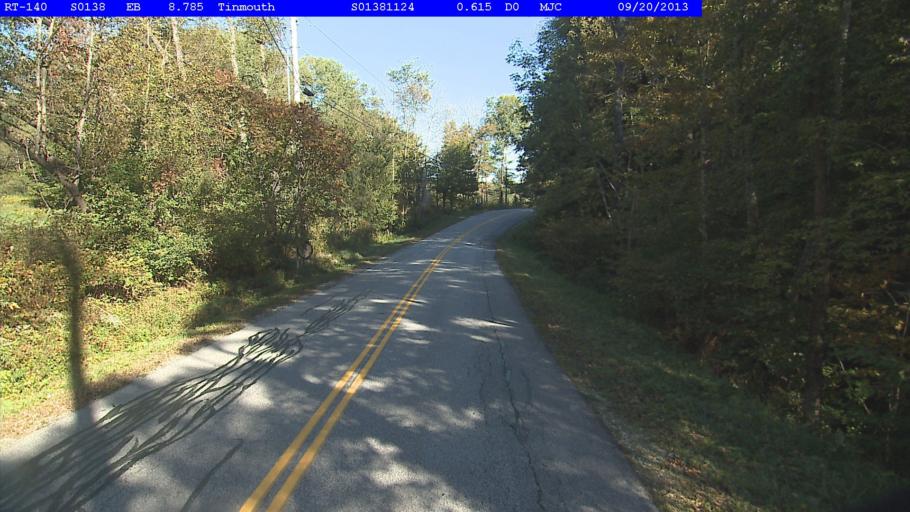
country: US
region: Vermont
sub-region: Rutland County
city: West Rutland
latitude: 43.4779
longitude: -73.0676
